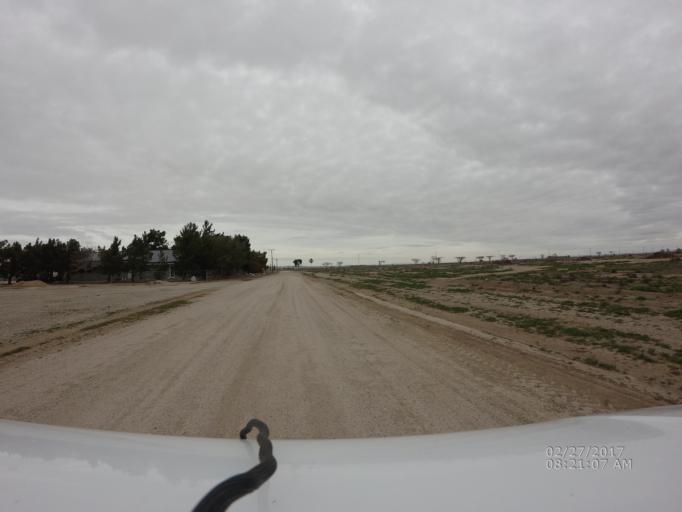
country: US
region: California
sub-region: Los Angeles County
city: Lancaster
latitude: 34.7319
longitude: -118.0143
